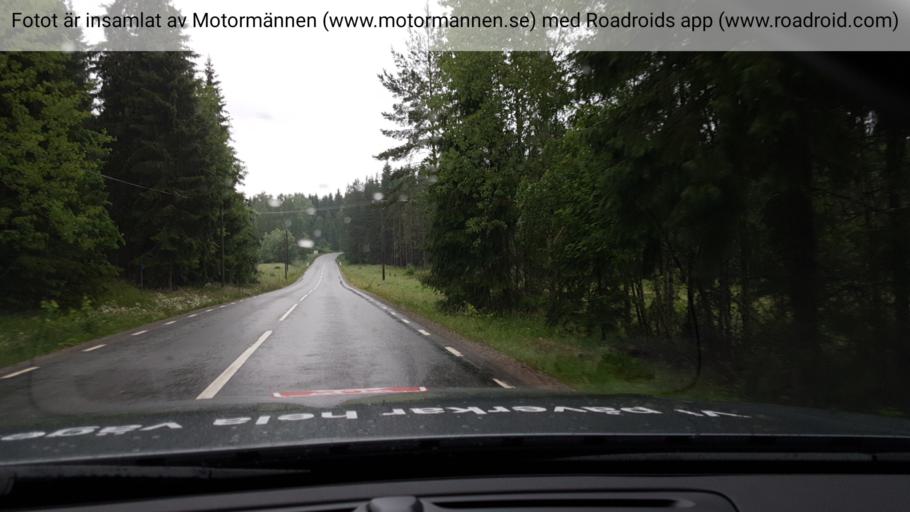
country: SE
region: Vaestmanland
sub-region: Norbergs Kommun
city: Norberg
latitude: 59.9722
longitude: 16.0185
